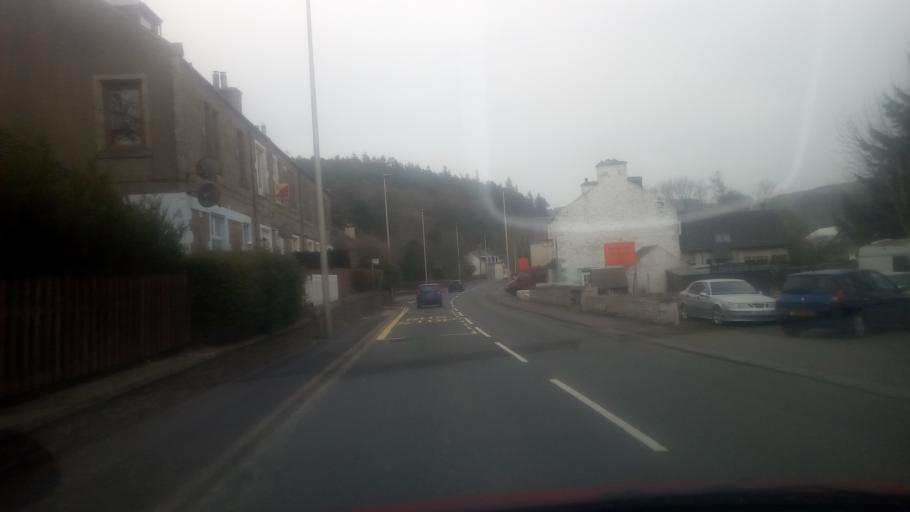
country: GB
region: Scotland
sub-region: The Scottish Borders
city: Galashiels
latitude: 55.6966
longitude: -2.8665
